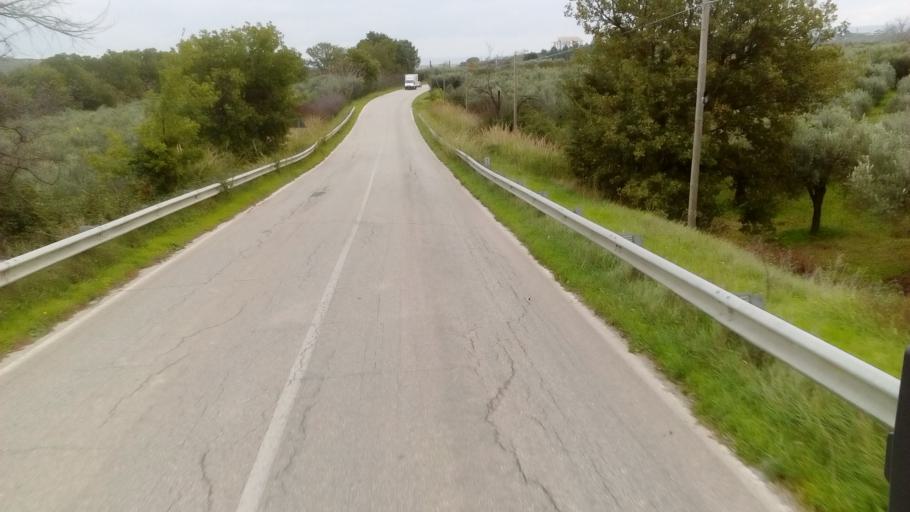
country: IT
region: Abruzzo
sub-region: Provincia di Chieti
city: San Salvo
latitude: 42.0580
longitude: 14.7052
